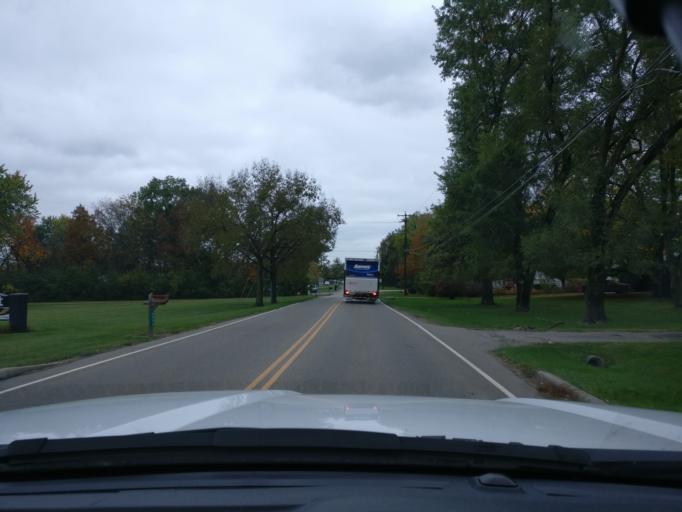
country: US
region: Ohio
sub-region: Butler County
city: Mayfield
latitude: 39.4812
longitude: -84.3370
